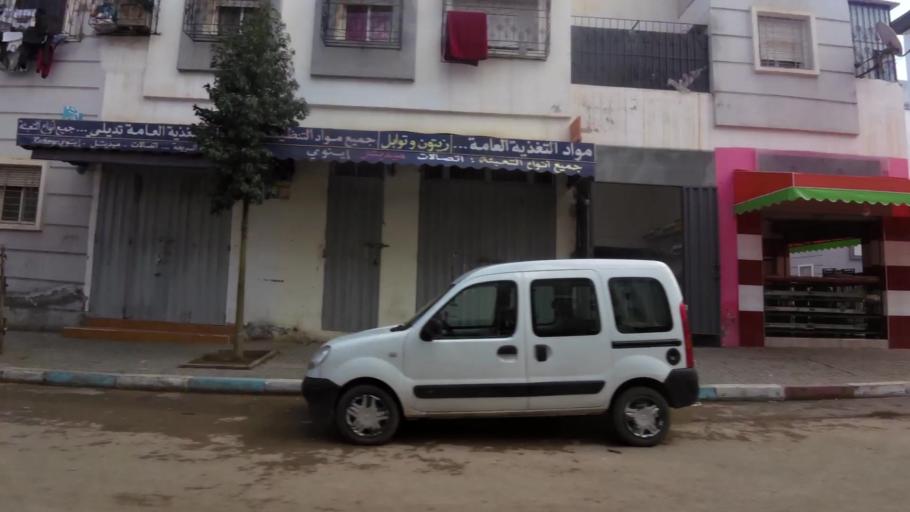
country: MA
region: Grand Casablanca
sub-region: Nouaceur
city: Dar Bouazza
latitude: 33.5338
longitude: -7.7200
